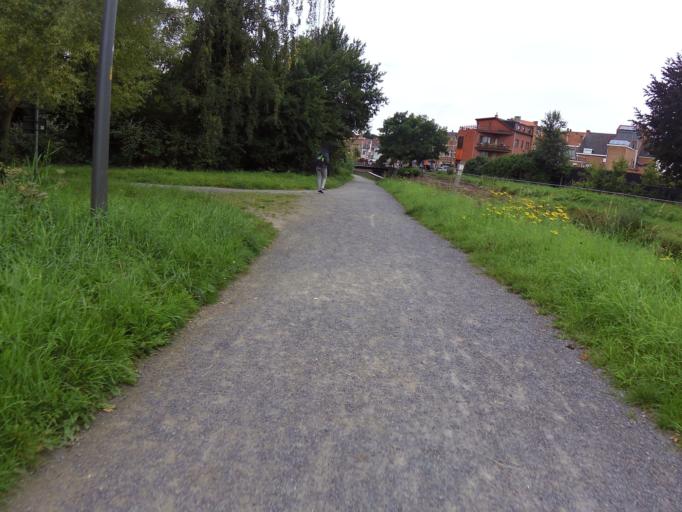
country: BE
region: Flanders
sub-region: Provincie Vlaams-Brabant
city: Aarschot
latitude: 50.9858
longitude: 4.8390
